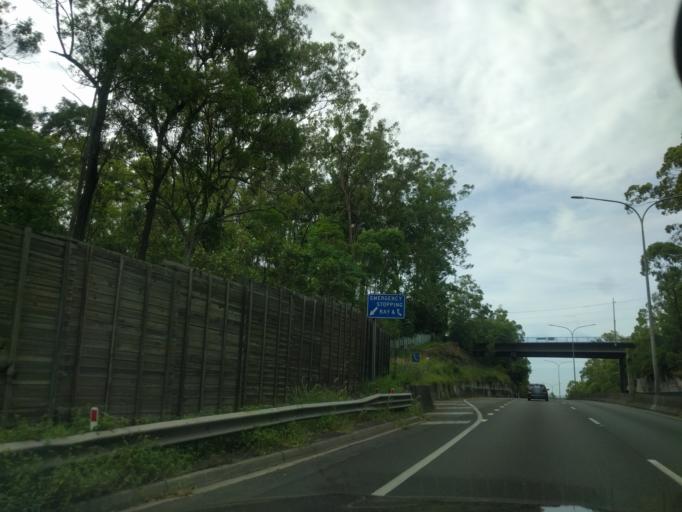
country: AU
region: Queensland
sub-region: Brisbane
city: Kenmore Hills
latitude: -27.5232
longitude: 152.9479
